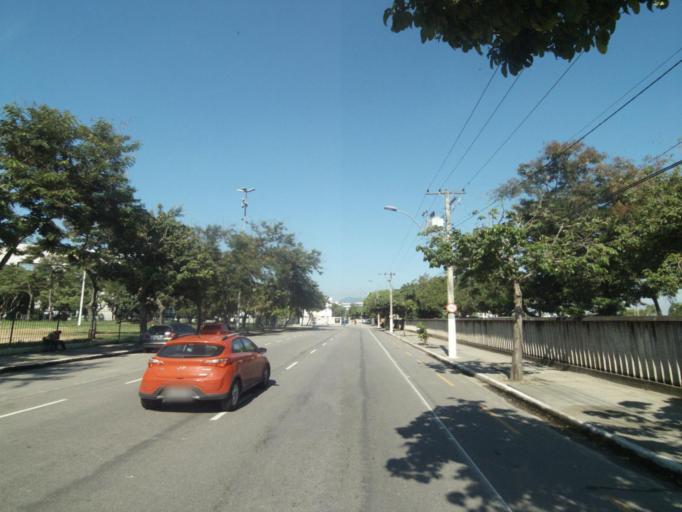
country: BR
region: Rio de Janeiro
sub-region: Niteroi
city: Niteroi
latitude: -22.8967
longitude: -43.1290
